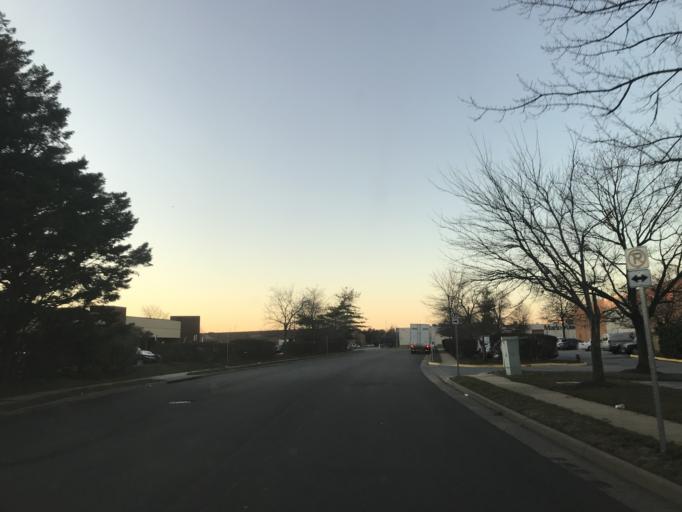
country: US
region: Virginia
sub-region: Fairfax County
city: Franconia
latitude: 38.7965
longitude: -77.1641
